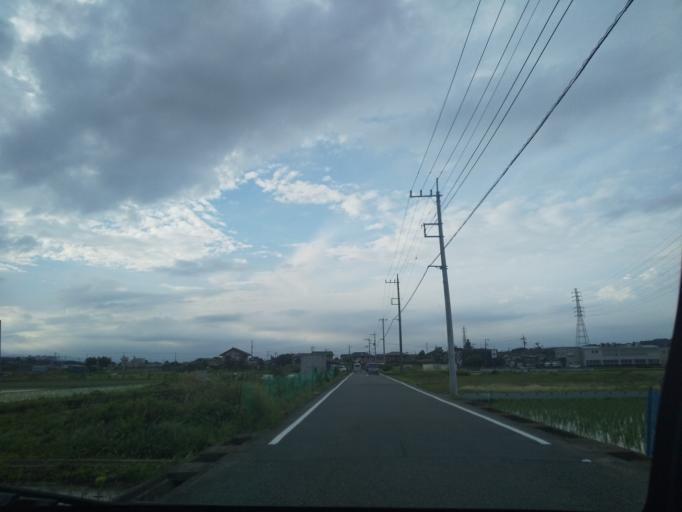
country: JP
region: Kanagawa
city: Zama
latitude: 35.4935
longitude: 139.3853
